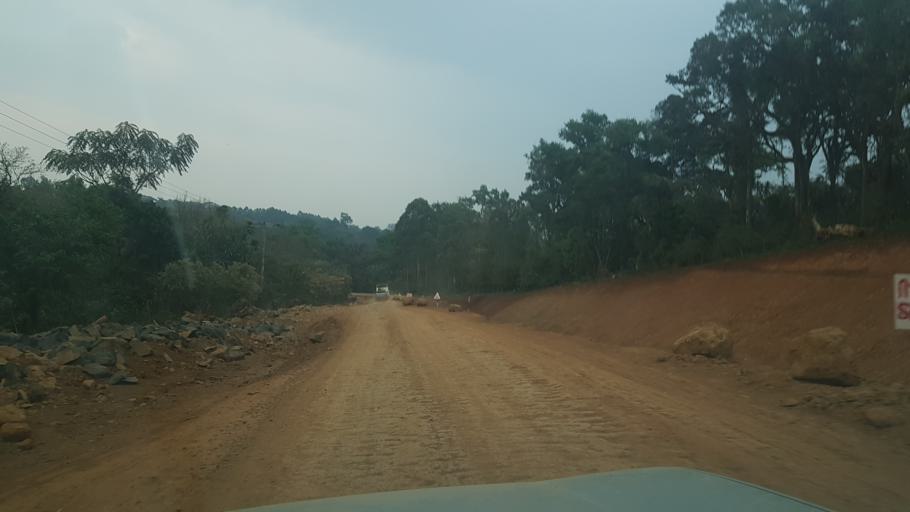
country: ET
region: Oromiya
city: Gore
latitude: 7.9036
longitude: 35.5028
